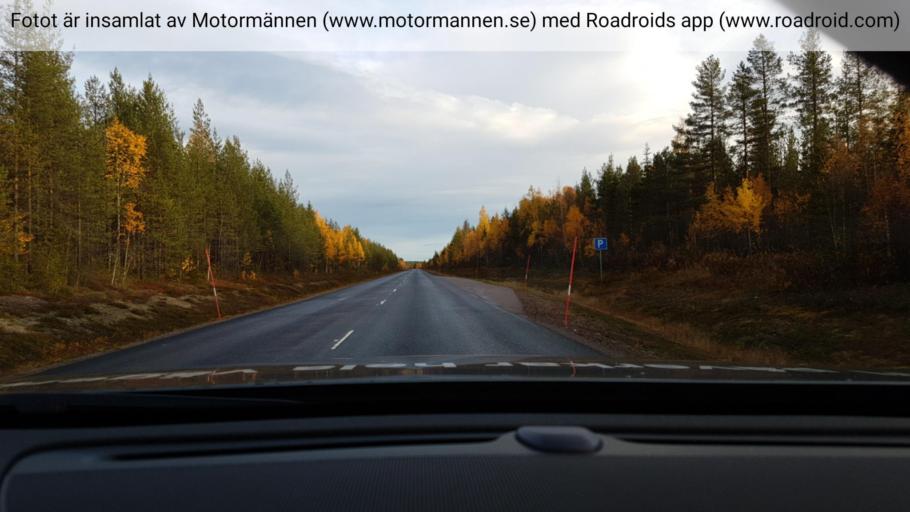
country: SE
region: Norrbotten
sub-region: Overkalix Kommun
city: OEverkalix
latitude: 66.9989
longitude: 22.5641
